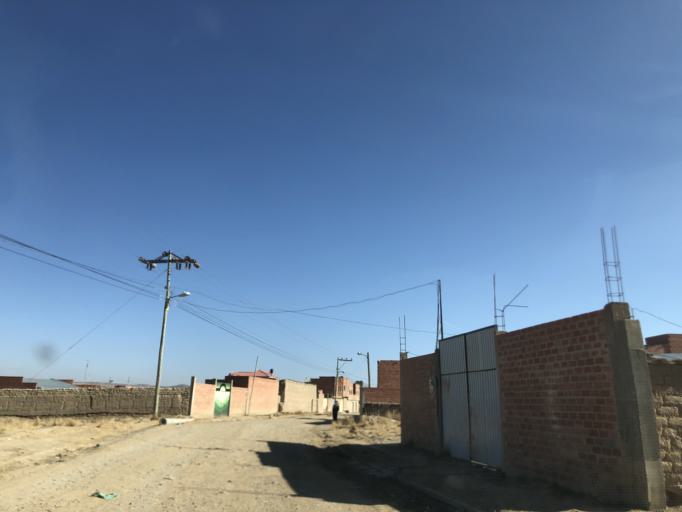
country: BO
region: La Paz
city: La Paz
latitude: -16.5399
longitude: -68.3837
